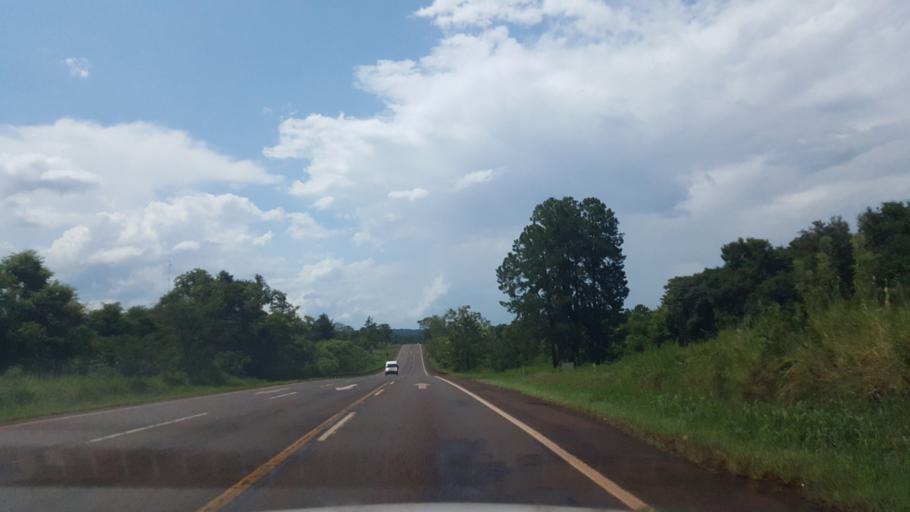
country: AR
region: Misiones
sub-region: Departamento de Eldorado
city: Eldorado
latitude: -26.3695
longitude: -54.6236
